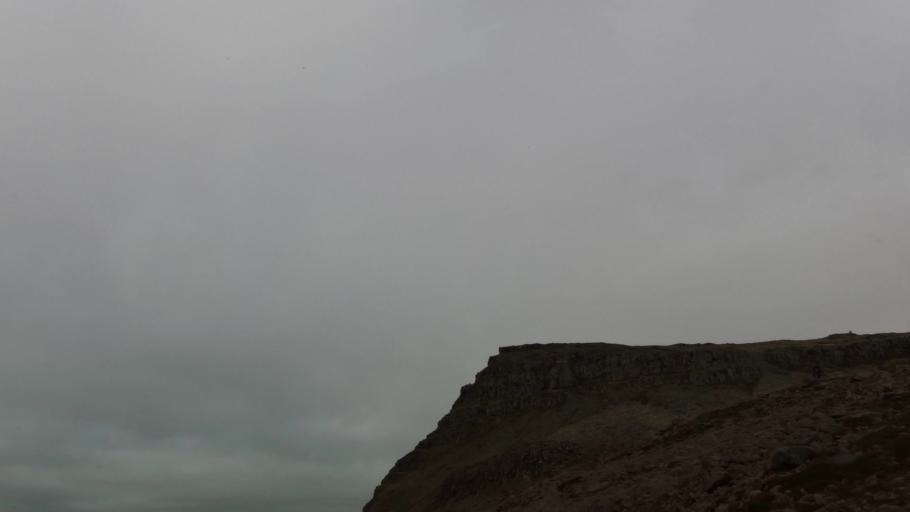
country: IS
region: West
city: Olafsvik
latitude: 65.5075
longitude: -24.5135
